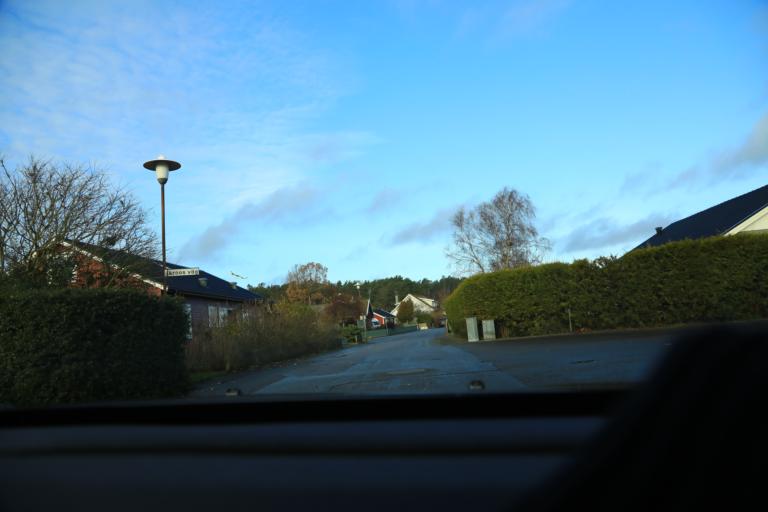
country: SE
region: Halland
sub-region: Varbergs Kommun
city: Varberg
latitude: 57.1723
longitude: 12.2236
